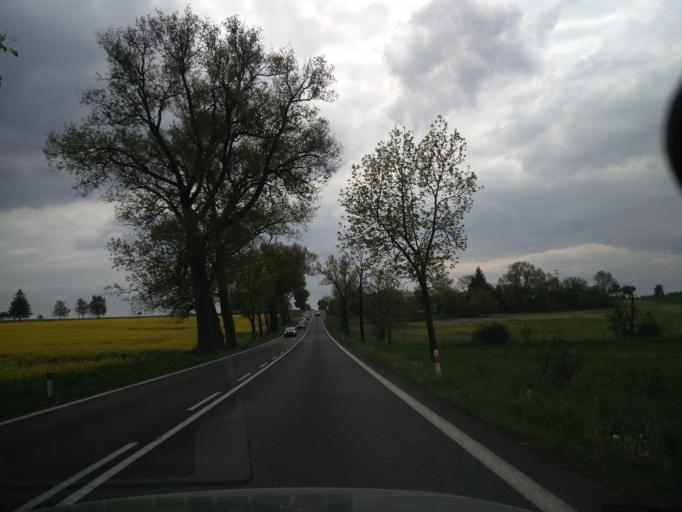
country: CZ
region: Central Bohemia
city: Milin
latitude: 49.6064
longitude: 14.0611
